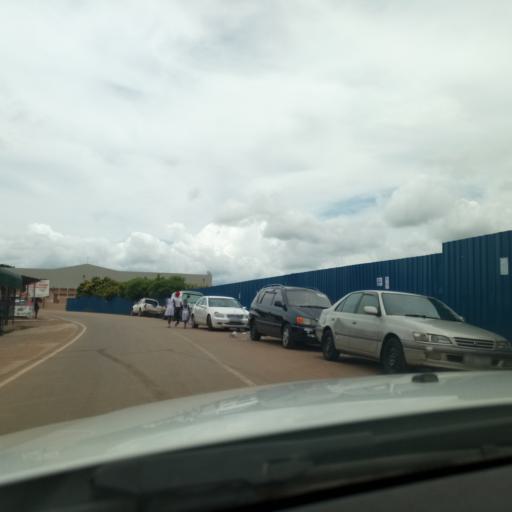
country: ZM
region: Lusaka
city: Lusaka
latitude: -15.4449
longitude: 28.3189
